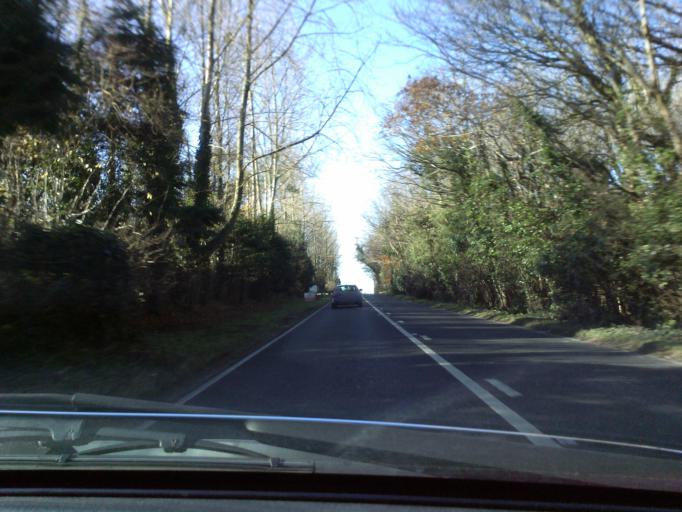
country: GB
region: England
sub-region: Dorset
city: Dorchester
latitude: 50.7125
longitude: -2.5116
